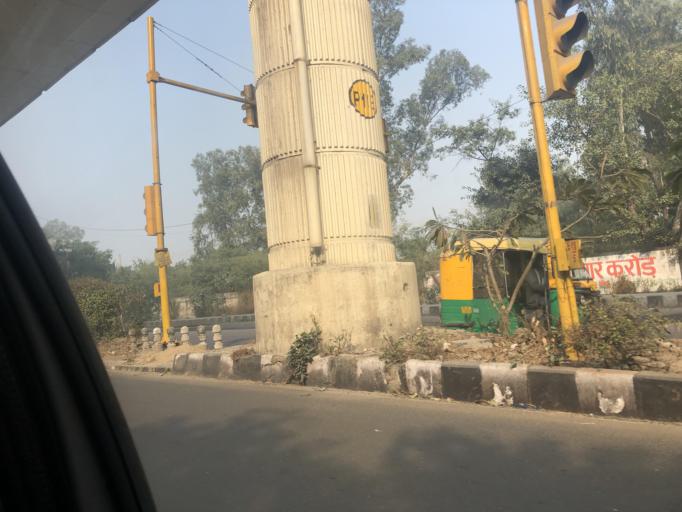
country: IN
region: NCT
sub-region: North West Delhi
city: Pitampura
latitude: 28.6744
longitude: 77.1344
